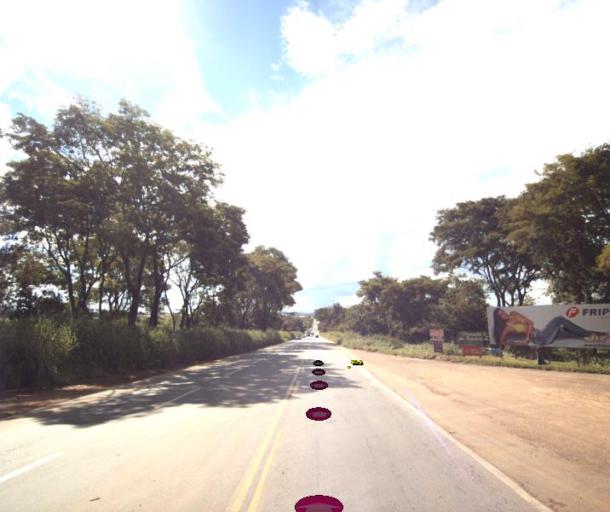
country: BR
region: Goias
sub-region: Jaragua
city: Jaragua
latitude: -15.7705
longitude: -49.3084
